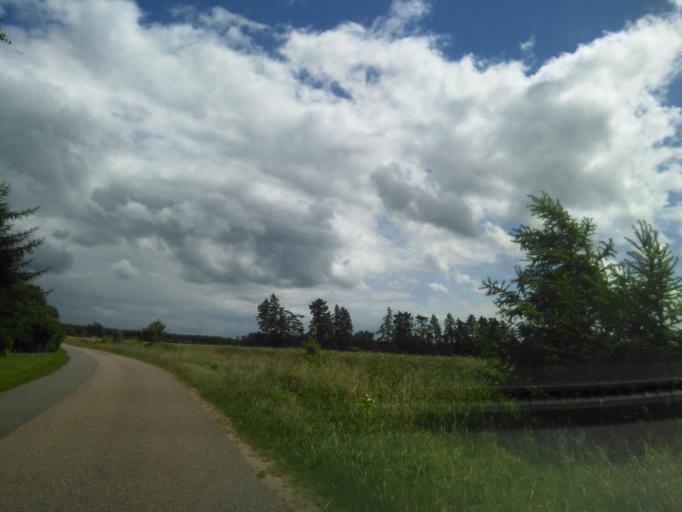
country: DK
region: Central Jutland
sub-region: Silkeborg Kommune
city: Virklund
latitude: 56.0363
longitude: 9.3975
